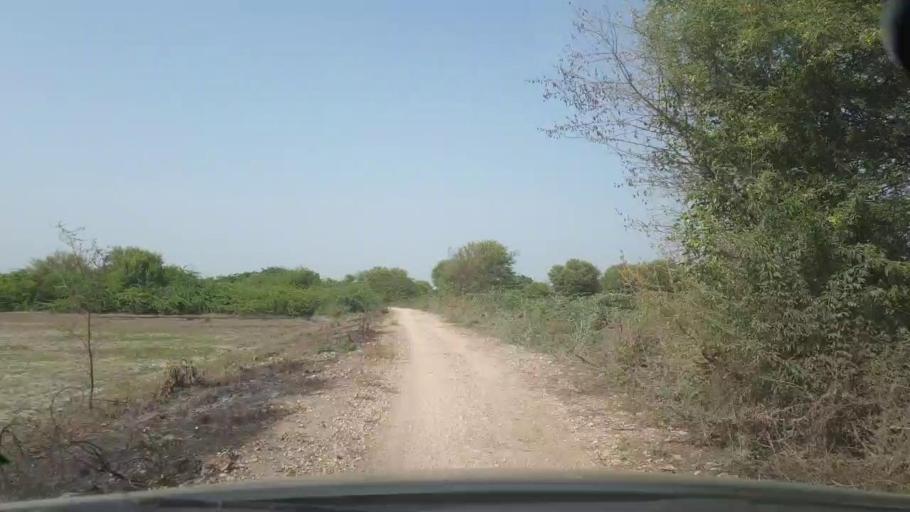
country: PK
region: Sindh
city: Naukot
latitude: 24.8000
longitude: 69.2410
